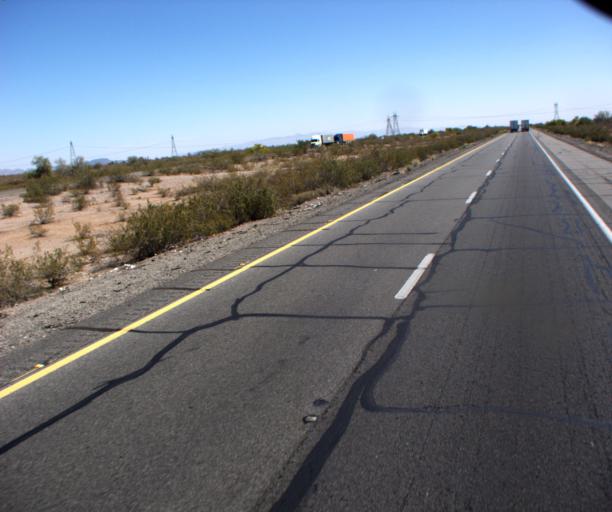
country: US
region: Arizona
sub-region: Maricopa County
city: Buckeye
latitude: 33.5158
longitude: -113.0431
